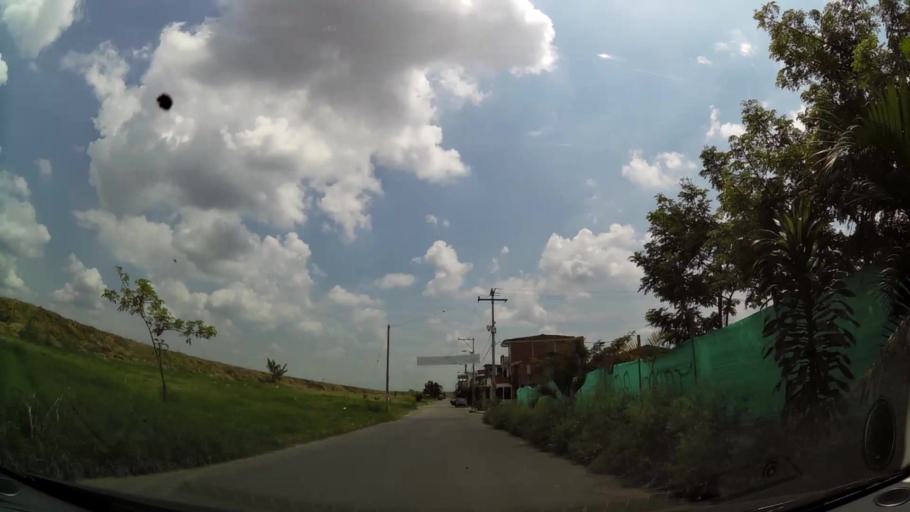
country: CO
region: Valle del Cauca
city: Cali
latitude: 3.4582
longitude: -76.4622
